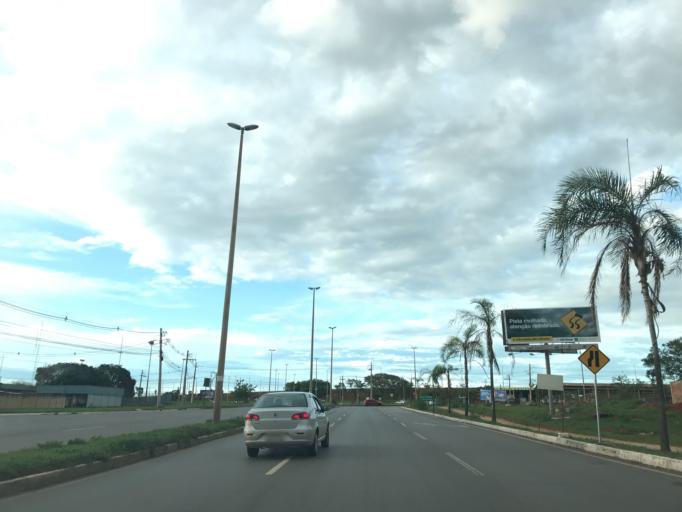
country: BR
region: Federal District
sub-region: Brasilia
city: Brasilia
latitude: -15.7986
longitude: -47.9712
